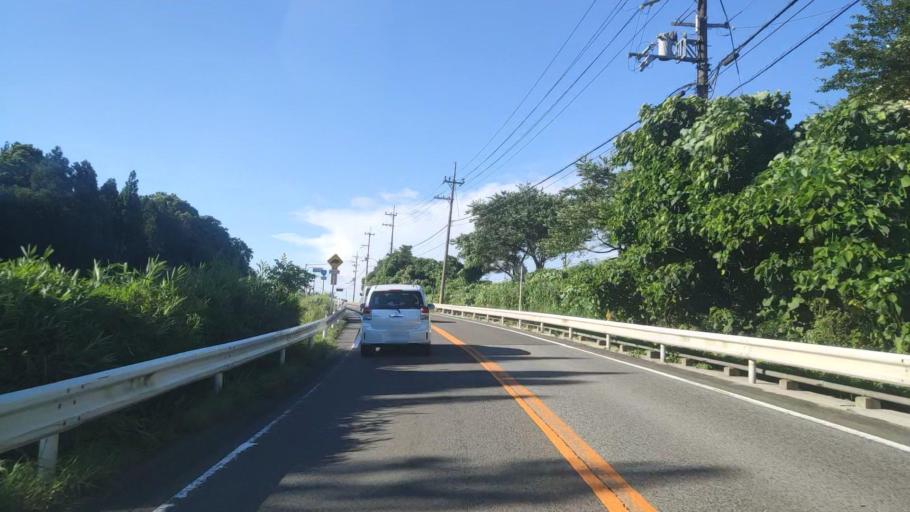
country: JP
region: Shiga Prefecture
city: Hino
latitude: 35.0661
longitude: 136.2493
